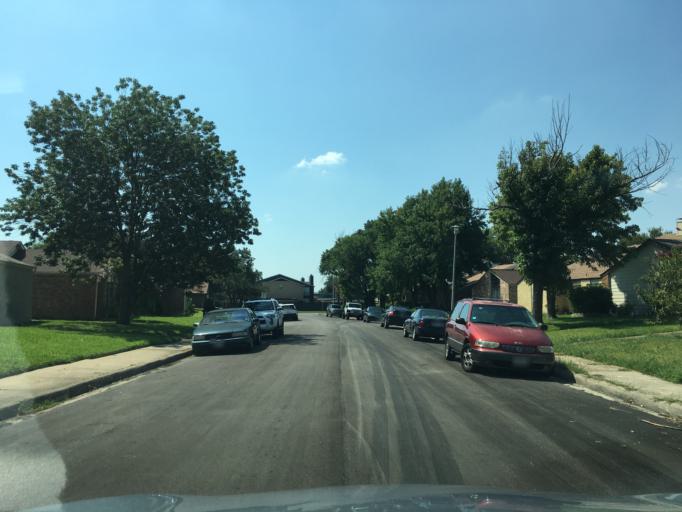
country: US
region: Texas
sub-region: Dallas County
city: Garland
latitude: 32.9337
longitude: -96.6617
